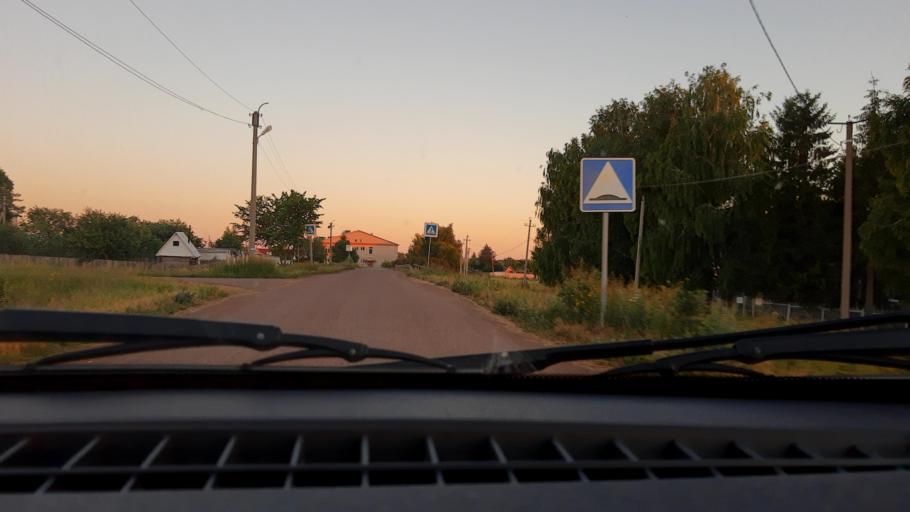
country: RU
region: Bashkortostan
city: Asanovo
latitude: 54.8902
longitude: 55.6241
